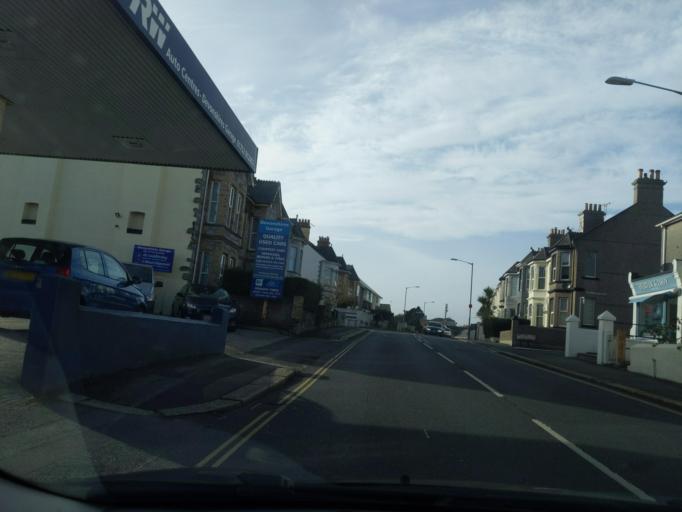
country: GB
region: England
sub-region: Cornwall
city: Torpoint
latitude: 50.3767
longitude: -4.2013
